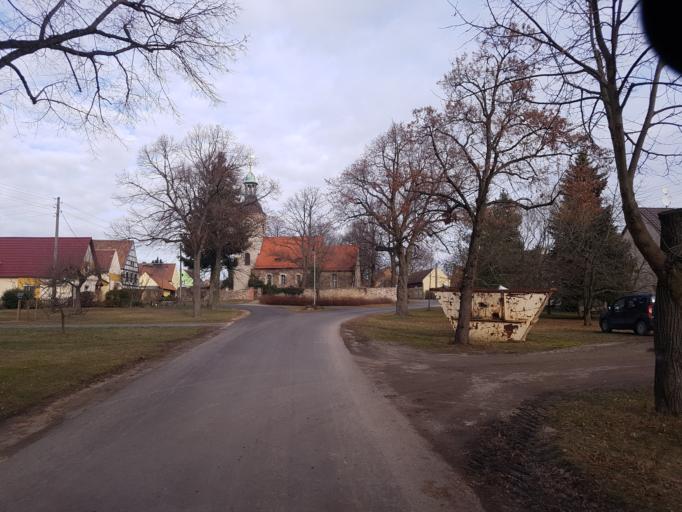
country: DE
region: Brandenburg
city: Finsterwalde
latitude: 51.6267
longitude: 13.7684
